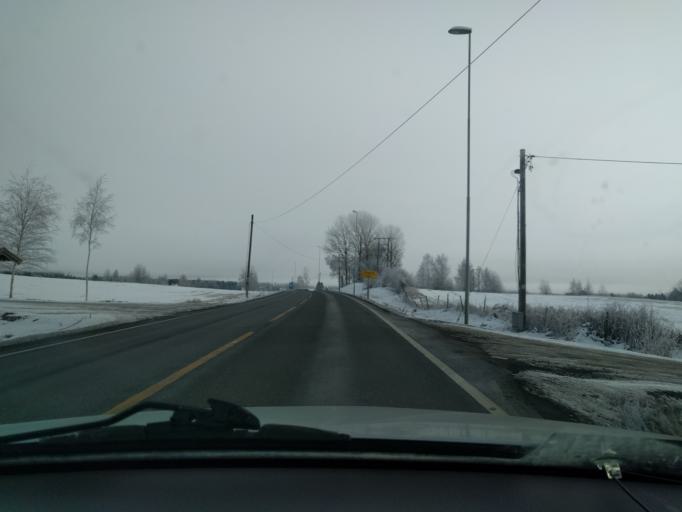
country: NO
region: Hedmark
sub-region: Loten
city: Loten
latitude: 60.8421
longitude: 11.3483
